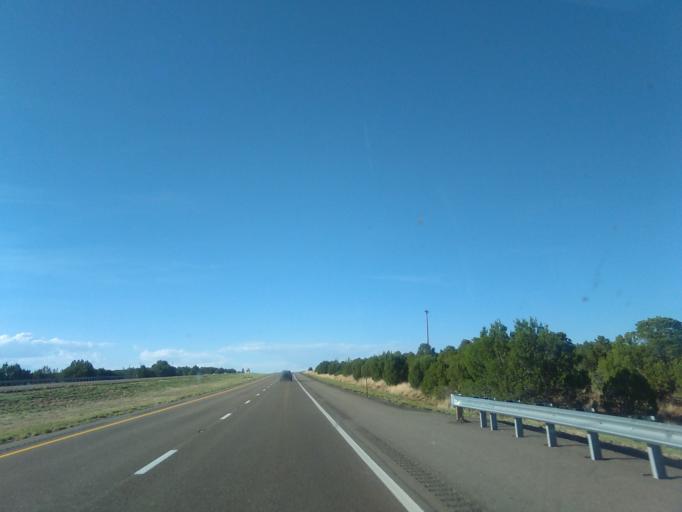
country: US
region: New Mexico
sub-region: San Miguel County
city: Las Vegas
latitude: 35.4719
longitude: -105.2753
